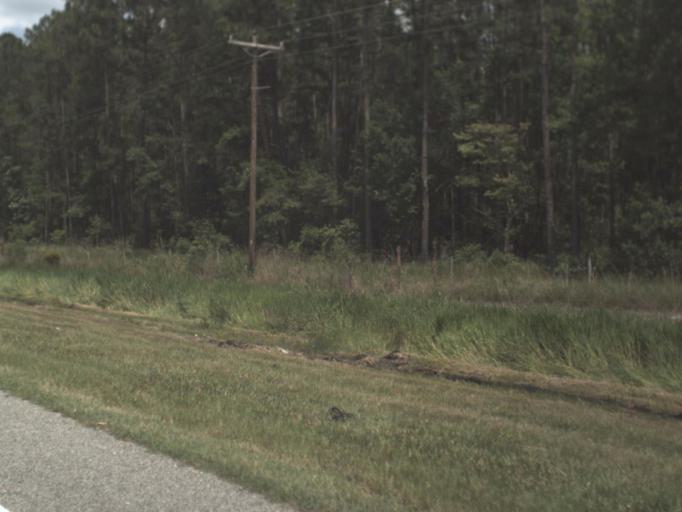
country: US
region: Florida
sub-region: Alachua County
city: Waldo
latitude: 29.7553
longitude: -82.2146
